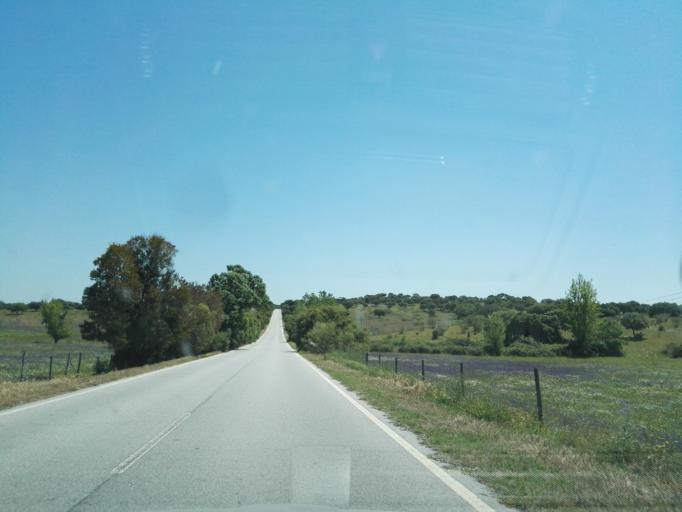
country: PT
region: Portalegre
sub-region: Elvas
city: Elvas
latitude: 38.9989
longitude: -7.1961
